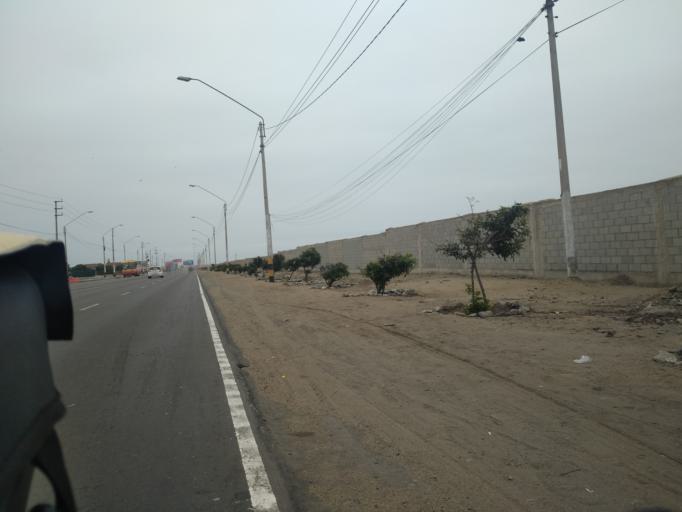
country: PE
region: La Libertad
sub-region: Provincia de Trujillo
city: Huanchaco
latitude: -8.0915
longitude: -79.1049
